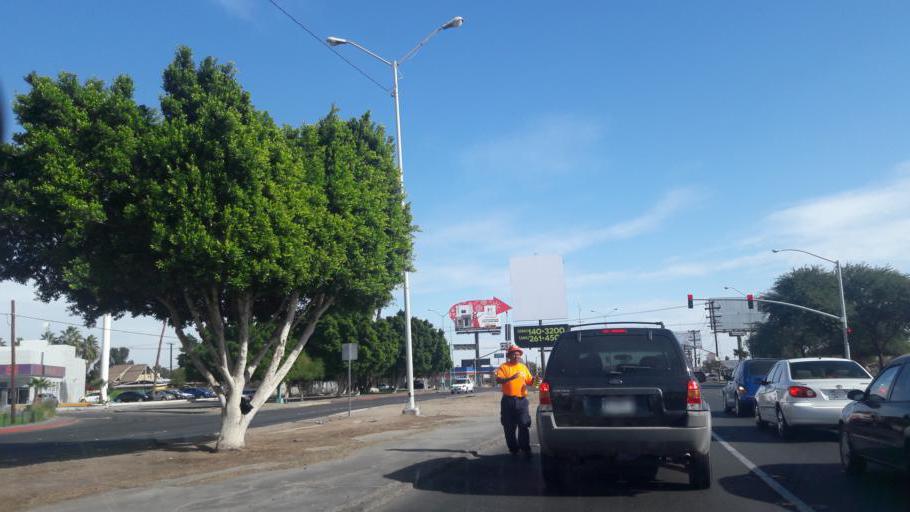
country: MX
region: Baja California
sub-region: Mexicali
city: Mexicali
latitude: 32.6238
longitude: -115.4919
